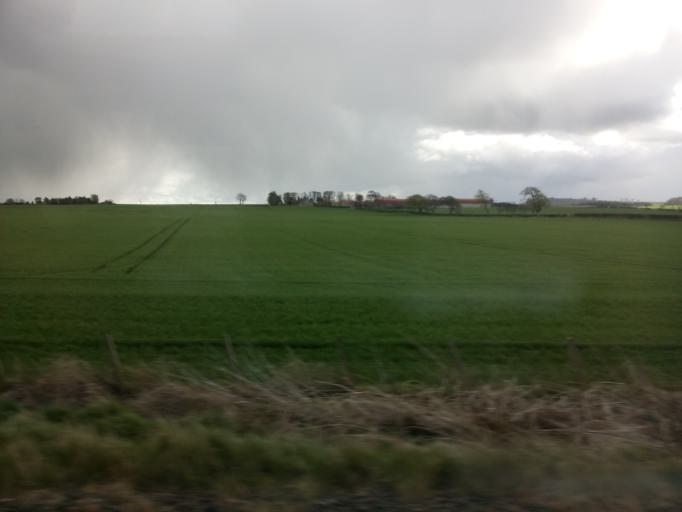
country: GB
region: Scotland
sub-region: East Lothian
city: North Berwick
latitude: 56.0081
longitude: -2.7532
